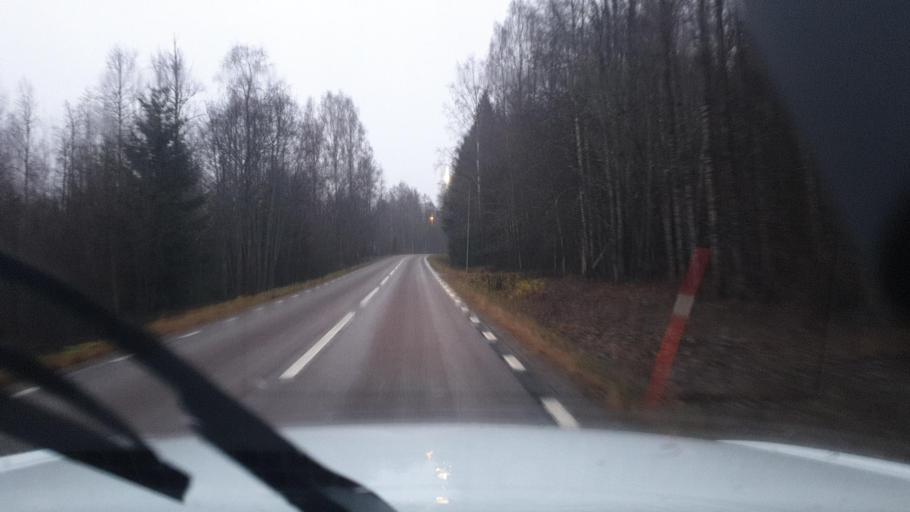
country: SE
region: Vaermland
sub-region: Sunne Kommun
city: Sunne
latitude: 59.8867
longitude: 12.9233
